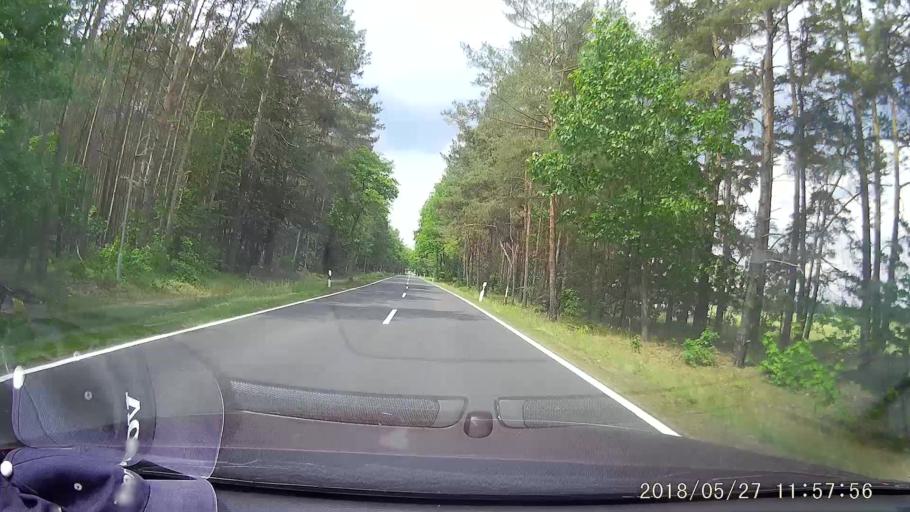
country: DE
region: Saxony
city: Mucka
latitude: 51.3090
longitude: 14.7173
